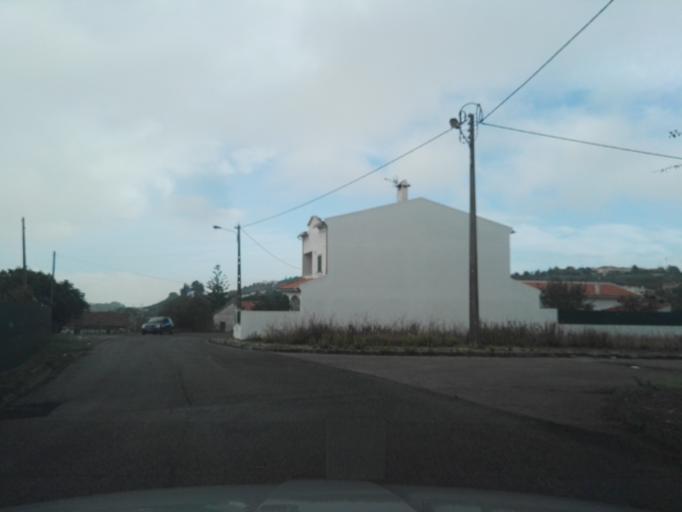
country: PT
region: Lisbon
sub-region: Vila Franca de Xira
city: Sao Joao dos Montes
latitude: 38.9621
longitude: -9.0238
